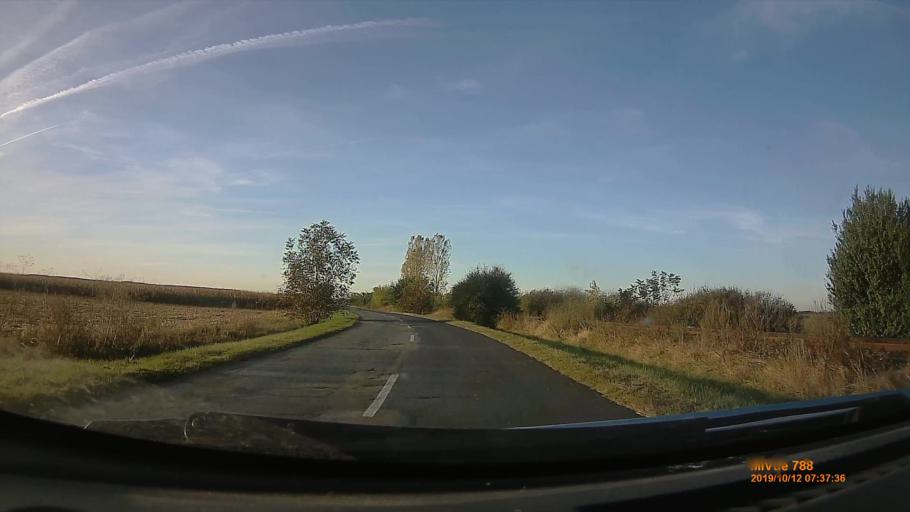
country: HU
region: Hajdu-Bihar
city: Pocsaj
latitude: 47.2345
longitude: 21.8133
